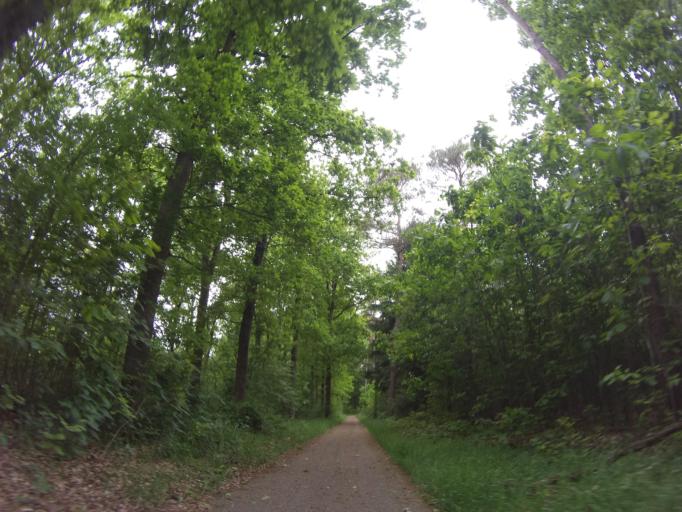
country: NL
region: Drenthe
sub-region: Gemeente Borger-Odoorn
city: Borger
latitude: 52.8697
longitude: 6.8135
